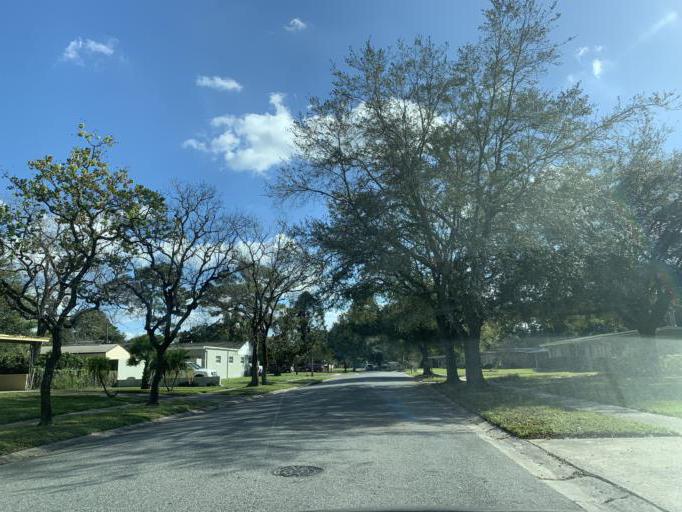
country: US
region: Florida
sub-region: Orange County
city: Eatonville
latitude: 28.6125
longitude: -81.4037
